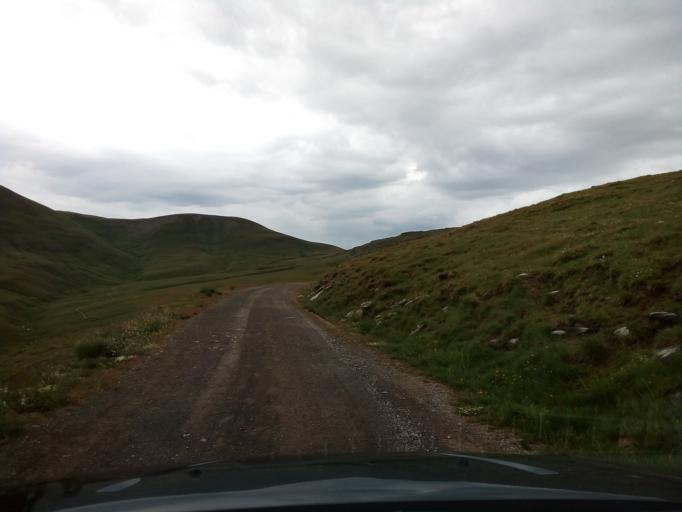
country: FR
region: Rhone-Alpes
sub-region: Departement de l'Isere
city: Mont-de-Lans
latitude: 45.0641
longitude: 6.2146
